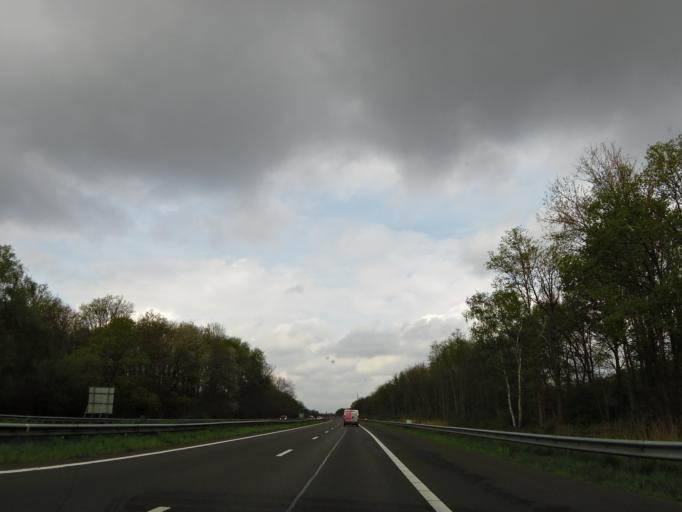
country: NL
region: Limburg
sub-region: Gemeente Leudal
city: Kelpen-Oler
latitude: 51.2281
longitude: 5.8031
